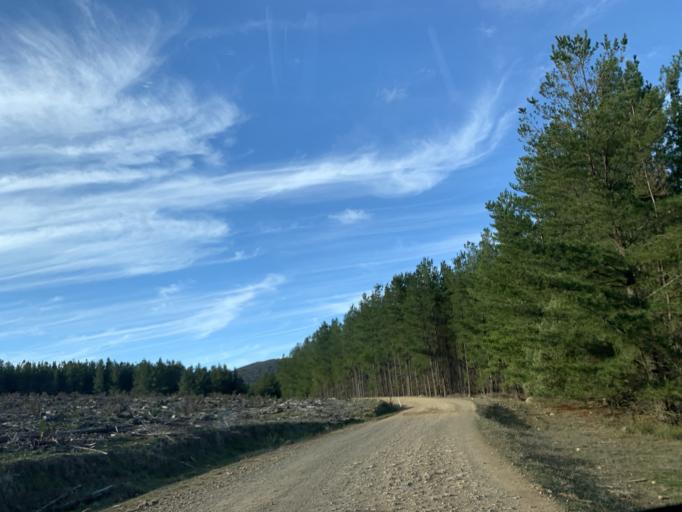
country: AU
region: Victoria
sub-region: Mansfield
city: Mansfield
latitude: -36.9100
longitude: 146.1119
